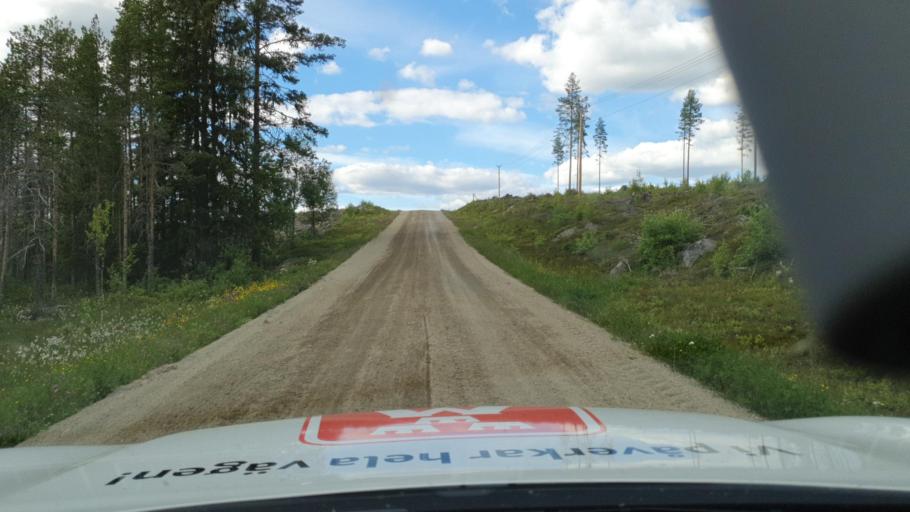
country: SE
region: Vaesterbotten
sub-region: Lycksele Kommun
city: Lycksele
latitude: 64.3012
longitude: 18.2880
